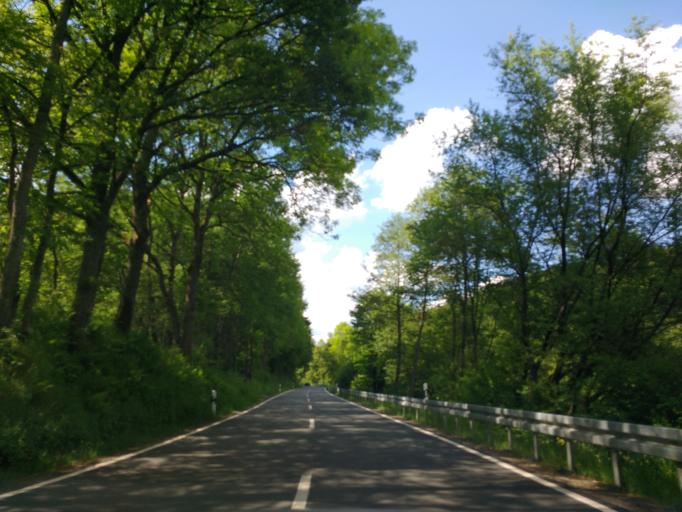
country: DE
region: Hesse
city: Hatzfeld
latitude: 50.9759
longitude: 8.5836
